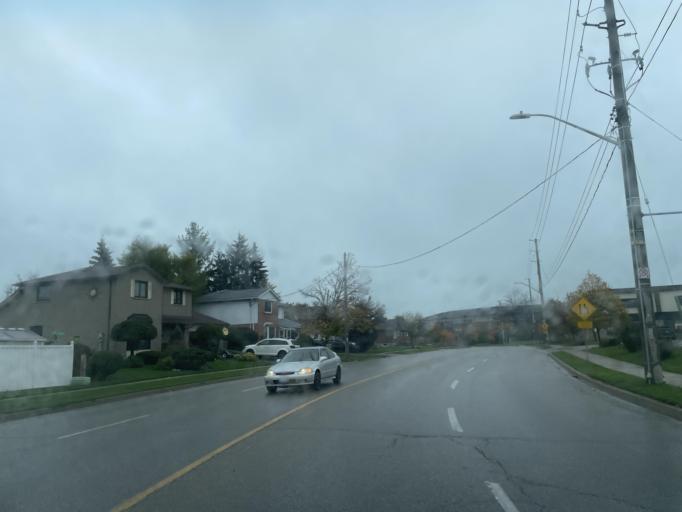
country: CA
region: Ontario
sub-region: Wellington County
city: Guelph
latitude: 43.5583
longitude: -80.2315
